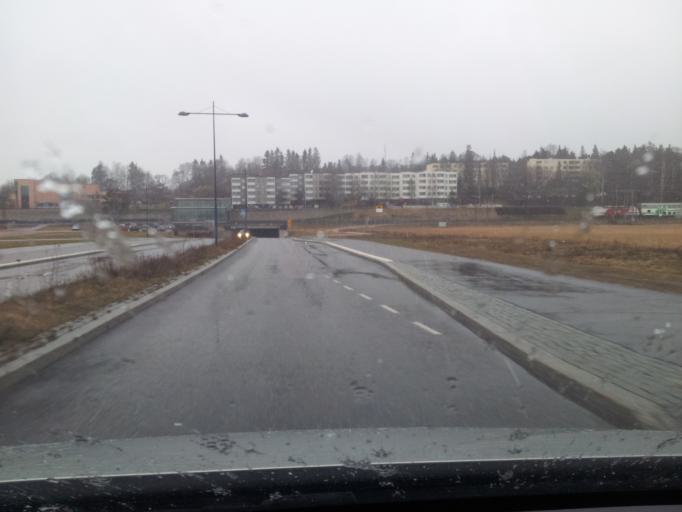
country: FI
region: Uusimaa
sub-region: Helsinki
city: Espoo
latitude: 60.1900
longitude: 24.6082
